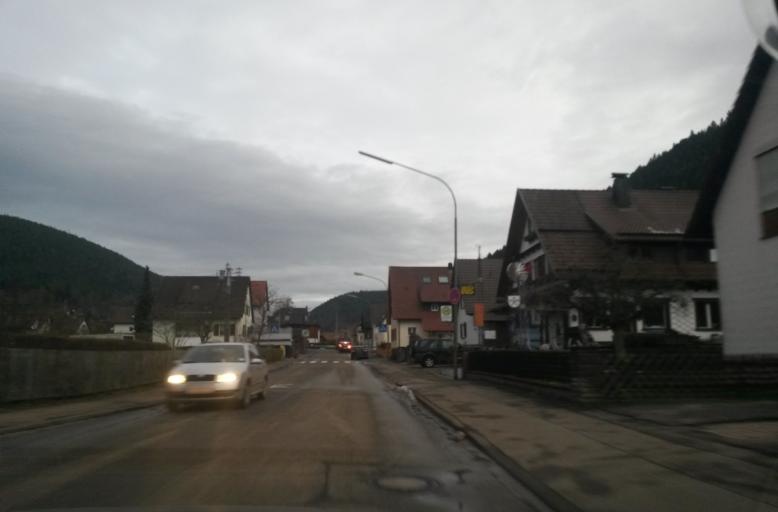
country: DE
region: Baden-Wuerttemberg
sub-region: Karlsruhe Region
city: Hofen an der Enz
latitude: 48.7769
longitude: 8.5768
